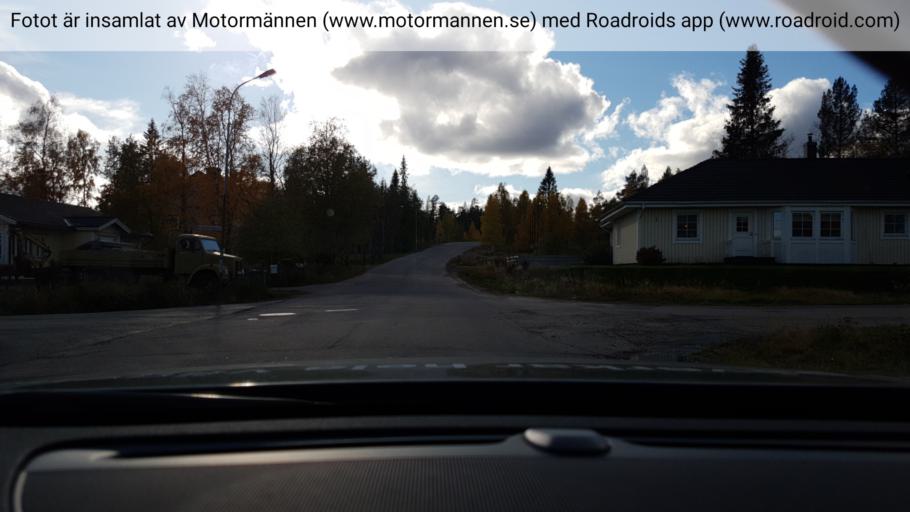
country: SE
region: Norrbotten
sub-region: Gallivare Kommun
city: Malmberget
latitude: 67.1814
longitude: 20.7239
